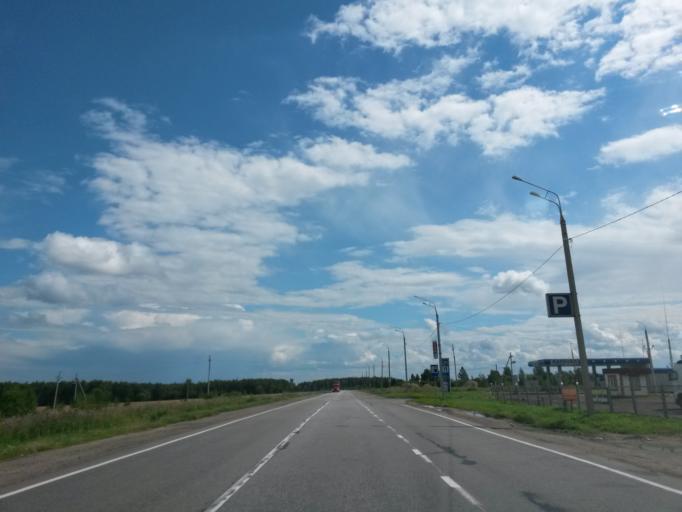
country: RU
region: Jaroslavl
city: Gavrilov-Yam
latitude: 57.2711
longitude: 39.9573
